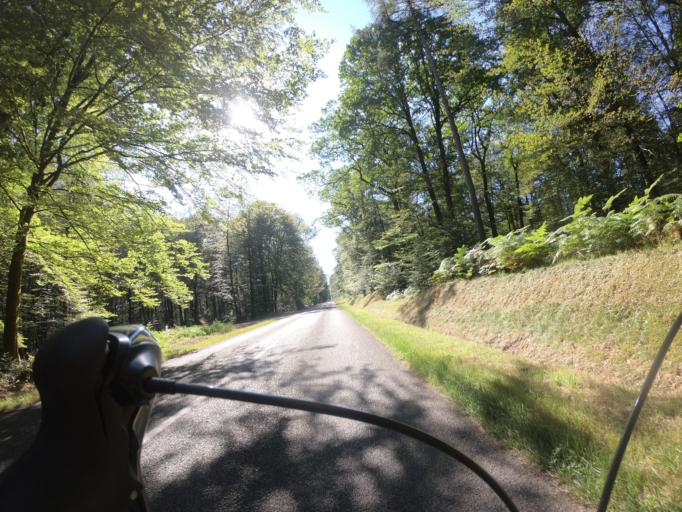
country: FR
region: Lower Normandy
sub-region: Departement de l'Orne
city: Juvigny-sous-Andaine
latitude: 48.5792
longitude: -0.4694
